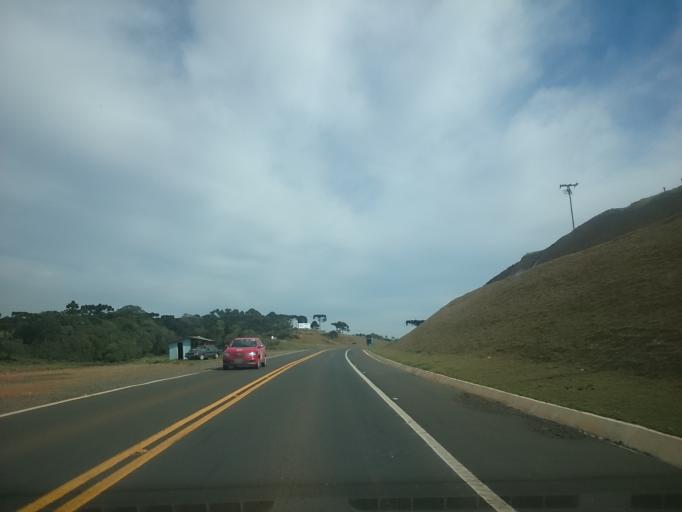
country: BR
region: Rio Grande do Sul
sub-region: Vacaria
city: Estrela
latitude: -28.0744
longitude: -50.5799
